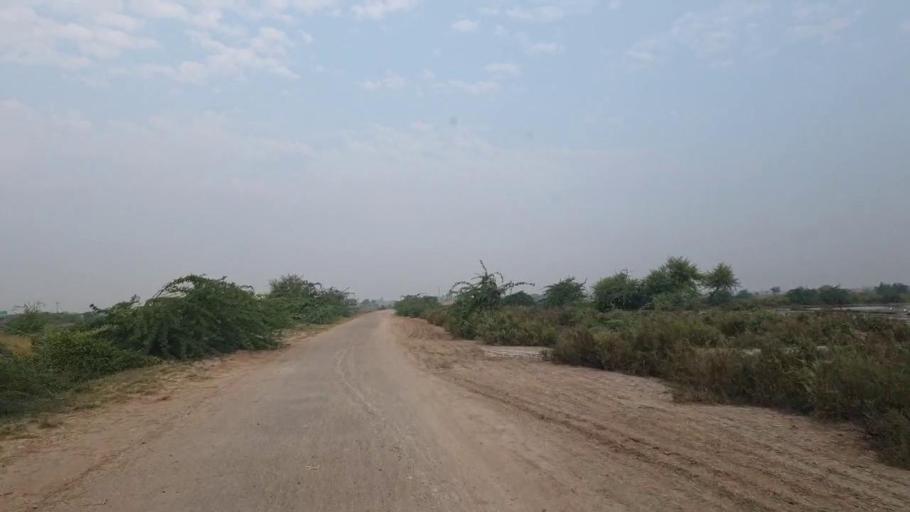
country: PK
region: Sindh
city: Tando Bago
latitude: 24.7798
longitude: 68.8906
